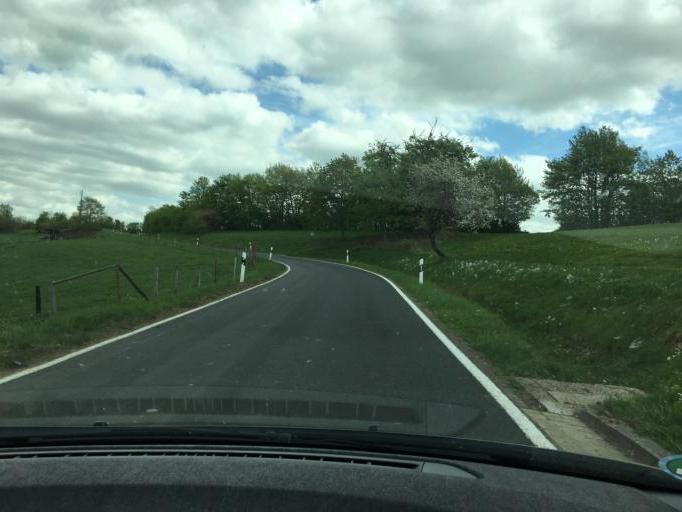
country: DE
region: Rheinland-Pfalz
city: Lind
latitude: 50.4929
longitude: 6.9282
